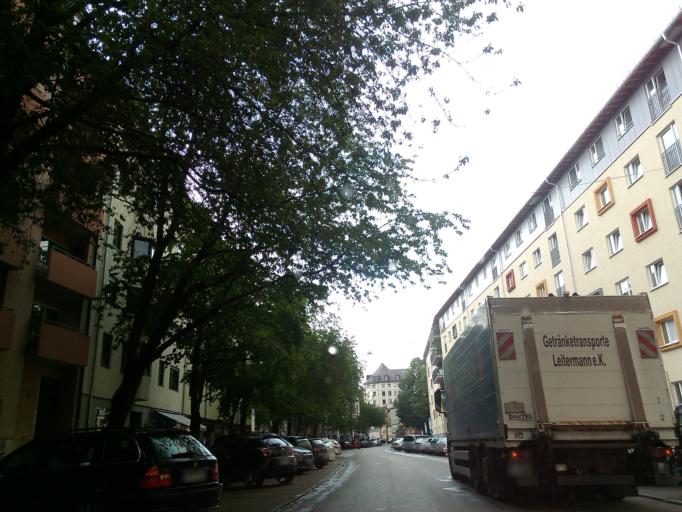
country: DE
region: Bavaria
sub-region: Upper Bavaria
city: Munich
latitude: 48.1294
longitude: 11.5867
